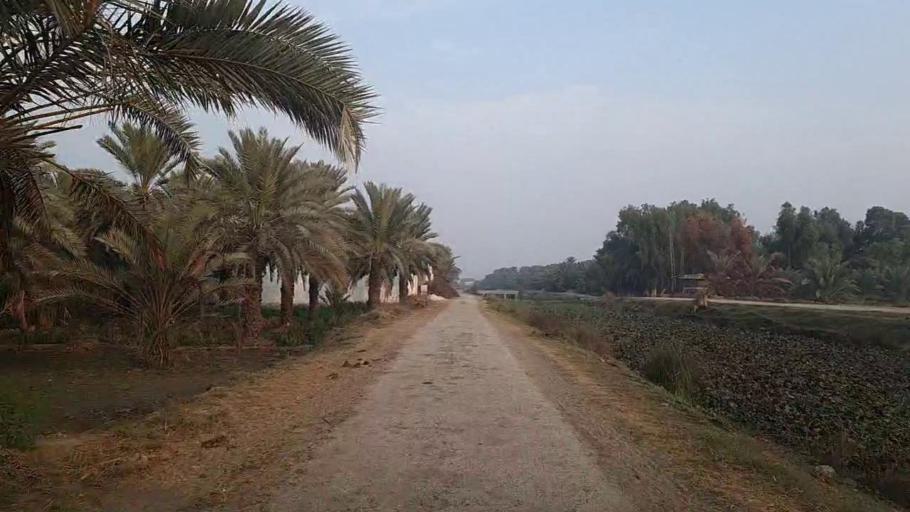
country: PK
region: Sindh
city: Kot Diji
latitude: 27.3582
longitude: 68.6509
